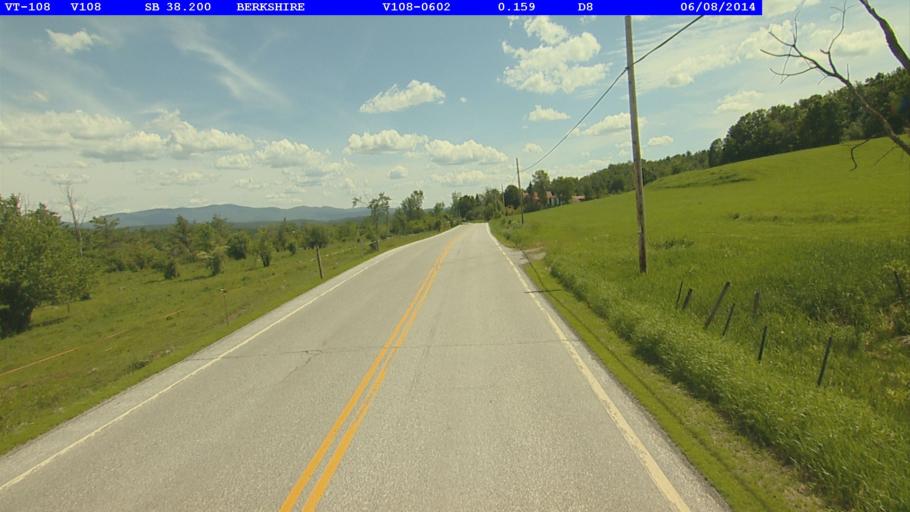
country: US
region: Vermont
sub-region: Franklin County
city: Enosburg Falls
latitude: 44.9273
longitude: -72.8099
